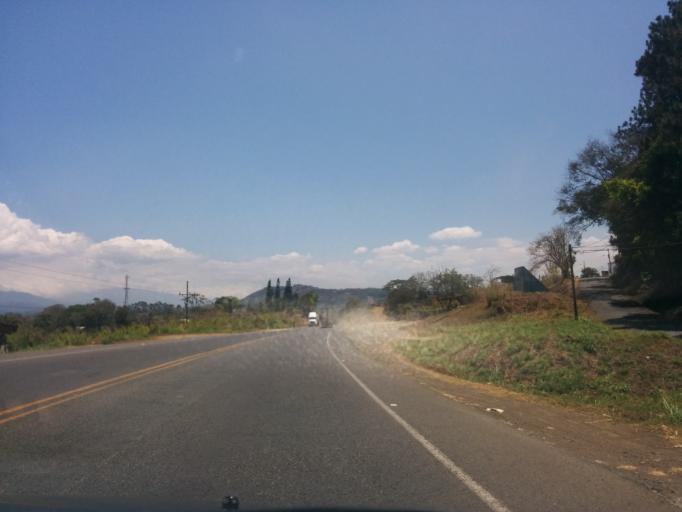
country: CR
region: Alajuela
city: San Rafael
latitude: 10.0759
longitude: -84.4789
